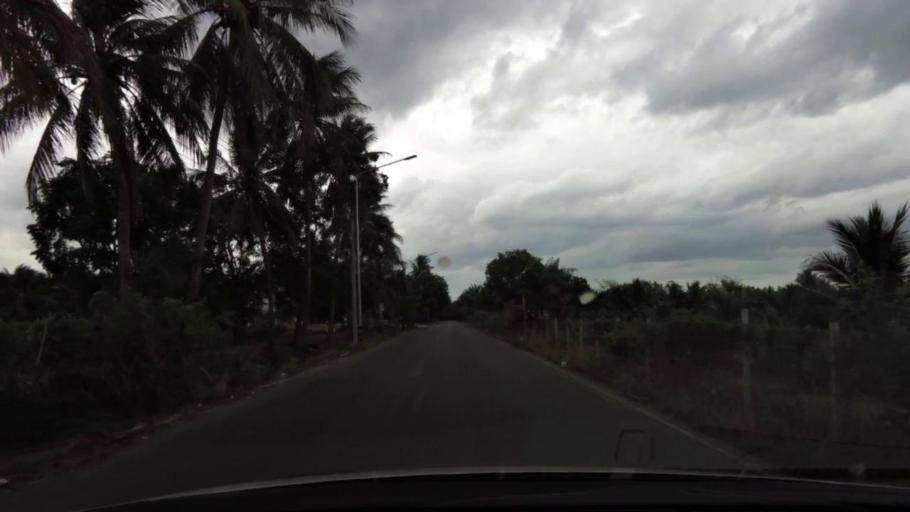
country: TH
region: Ratchaburi
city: Damnoen Saduak
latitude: 13.5730
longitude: 99.9813
